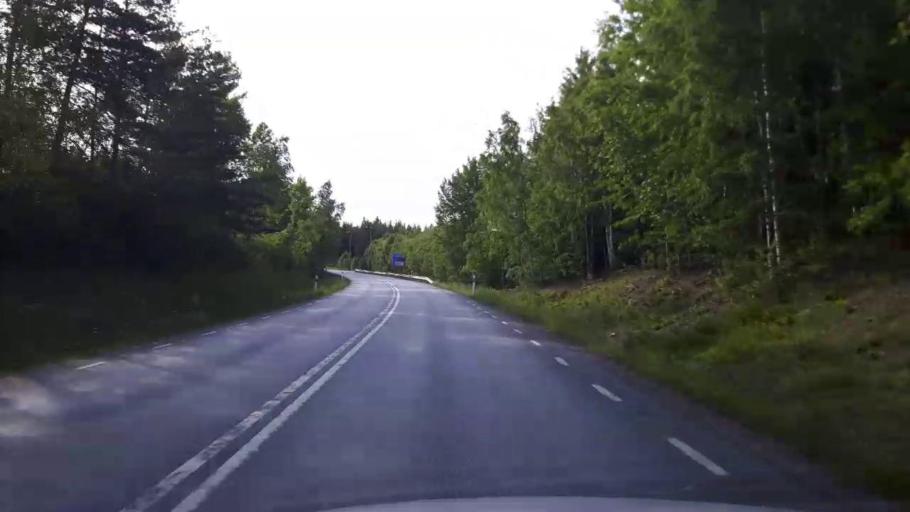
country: SE
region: Uppsala
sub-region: Habo Kommun
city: Balsta
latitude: 59.6512
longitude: 17.5607
